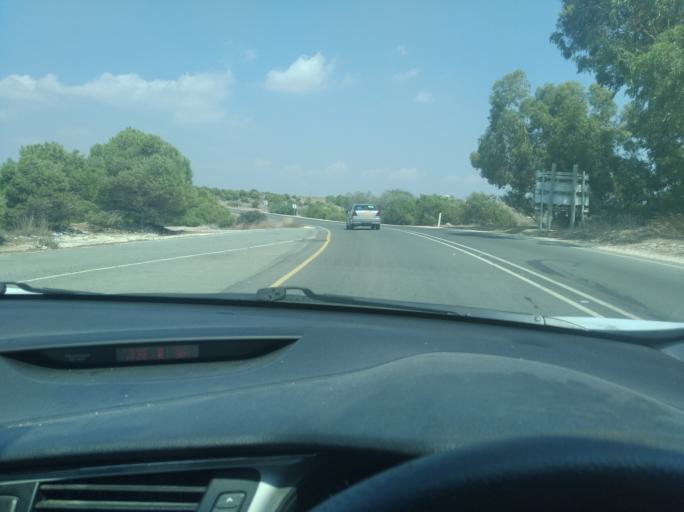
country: CY
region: Larnaka
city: Xylotymbou
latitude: 34.9823
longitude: 33.7838
